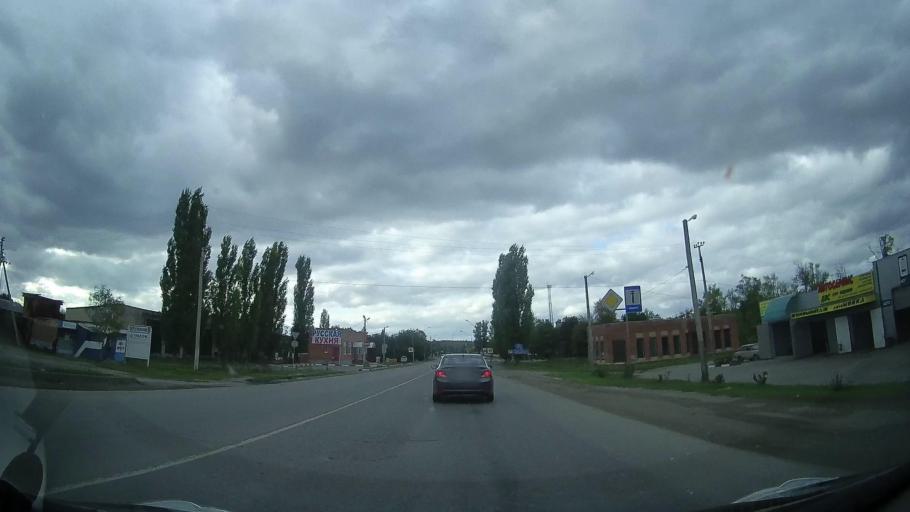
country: RU
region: Rostov
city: Kagal'nitskaya
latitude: 46.8774
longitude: 40.1567
